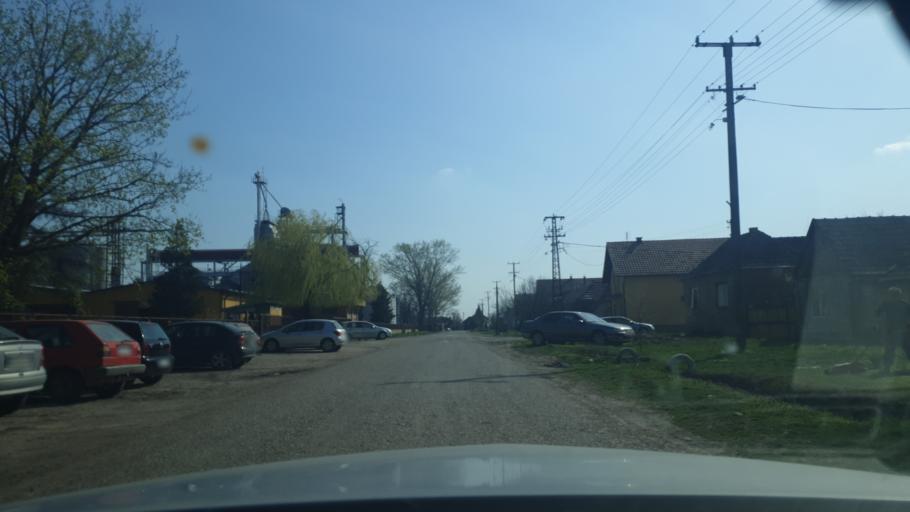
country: RS
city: Putinci
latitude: 45.0032
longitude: 19.9392
